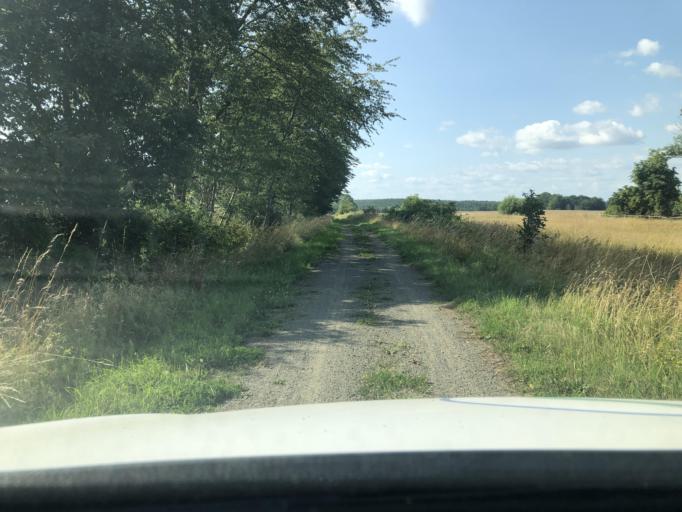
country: SE
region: Skane
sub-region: Kristianstads Kommun
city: Degeberga
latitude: 55.8189
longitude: 14.1221
